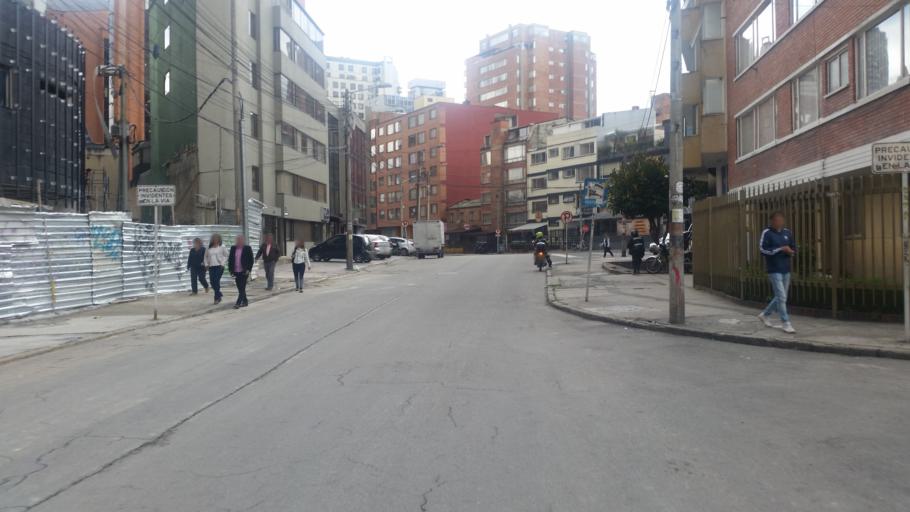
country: CO
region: Bogota D.C.
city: Bogota
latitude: 4.6421
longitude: -74.0635
